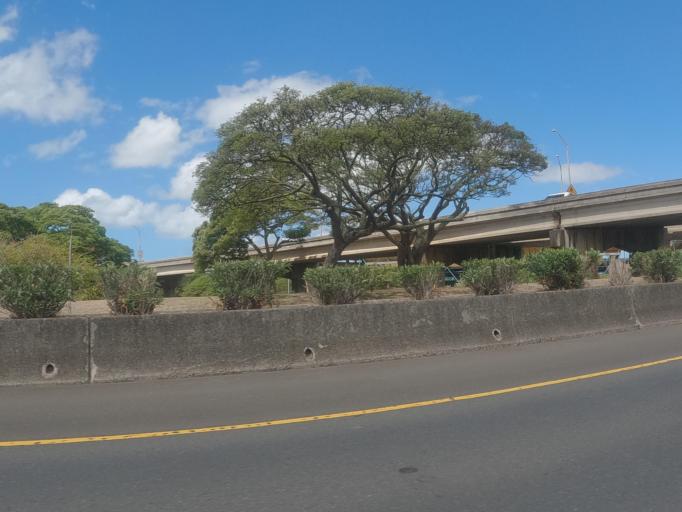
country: US
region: Hawaii
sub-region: Honolulu County
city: Halawa
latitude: 21.3739
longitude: -157.9265
